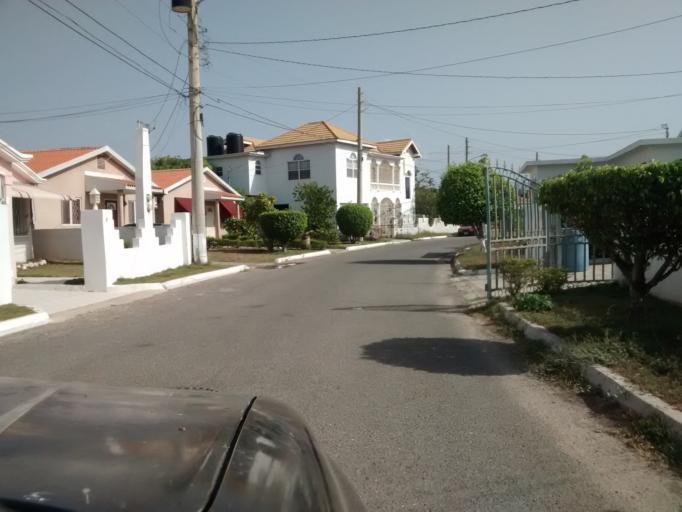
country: JM
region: Saint Catherine
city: Portmore
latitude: 17.9854
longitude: -76.8849
